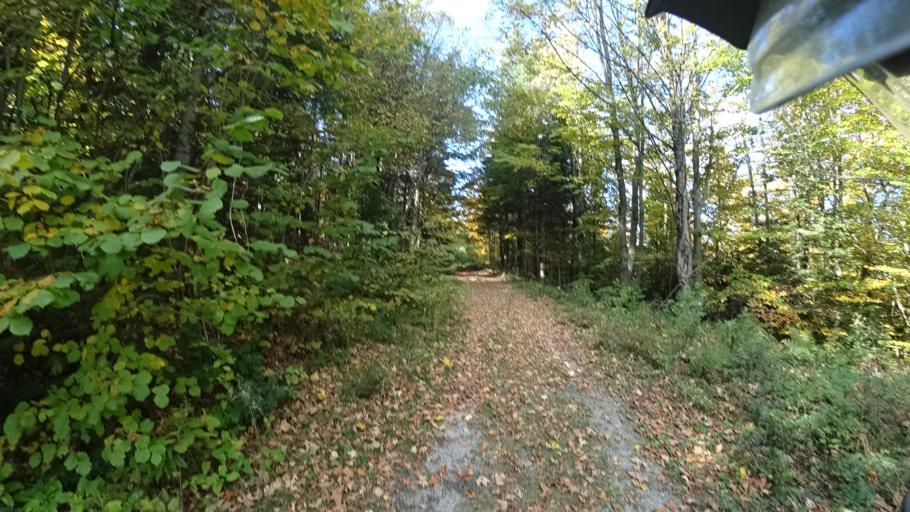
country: HR
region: Karlovacka
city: Plaski
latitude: 45.0707
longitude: 15.3256
